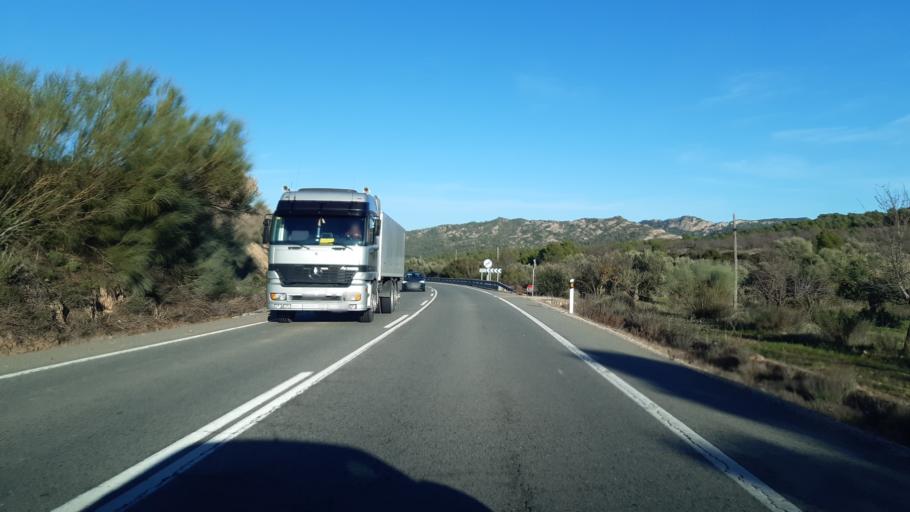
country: ES
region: Catalonia
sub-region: Provincia de Tarragona
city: la Fatarella
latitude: 41.1007
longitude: 0.5219
